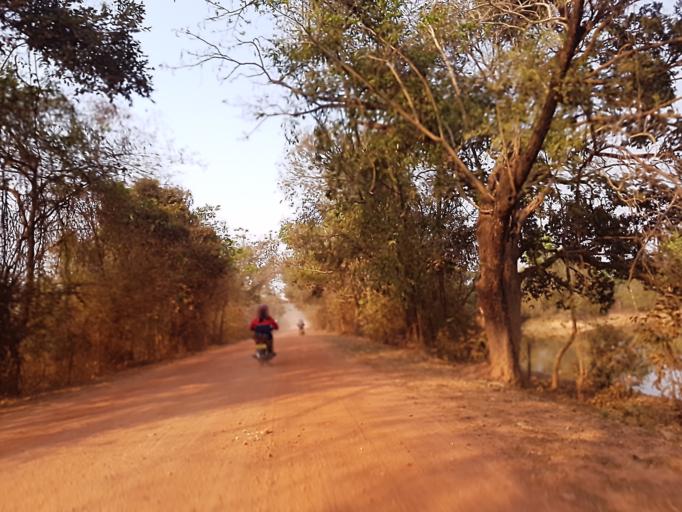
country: TH
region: Nong Khai
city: Phon Phisai
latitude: 18.0064
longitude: 102.9084
